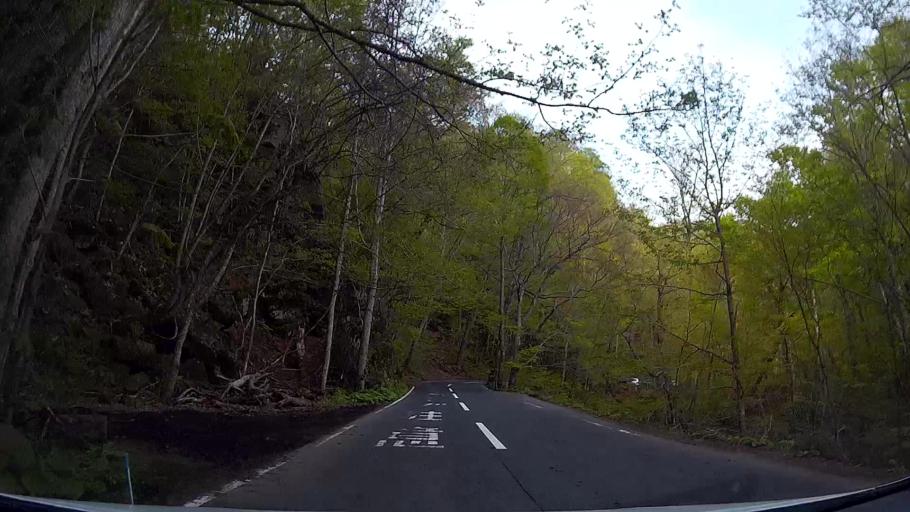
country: JP
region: Aomori
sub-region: Aomori Shi
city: Furudate
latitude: 40.5296
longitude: 140.9750
